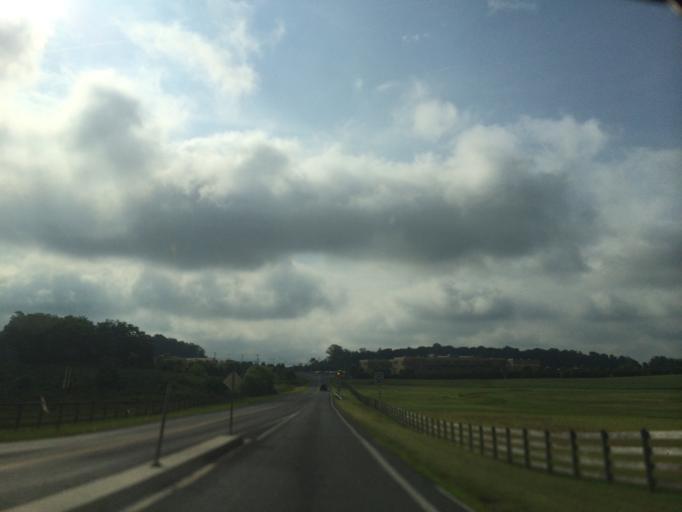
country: US
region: Maryland
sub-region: Carroll County
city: Sykesville
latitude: 39.3042
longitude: -77.0262
